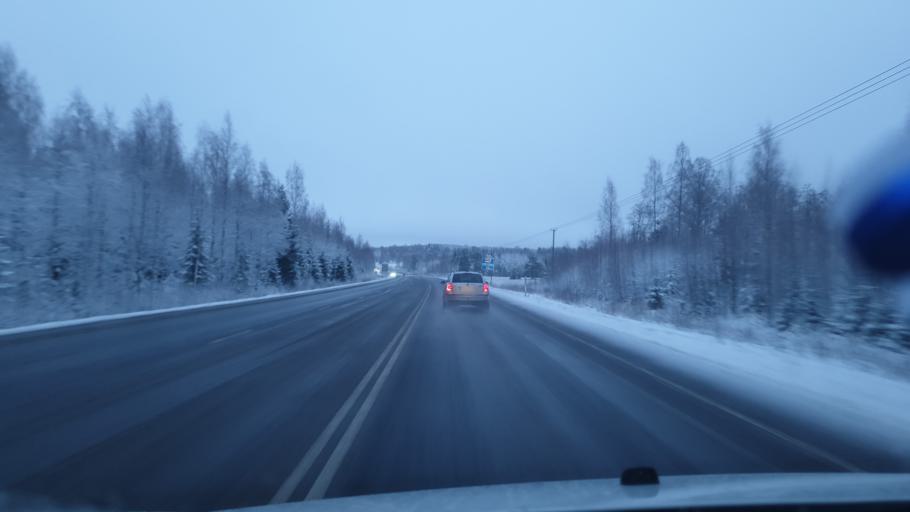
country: FI
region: Central Finland
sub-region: Saarijaervi-Viitasaari
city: Viitasaari
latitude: 63.1188
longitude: 25.7911
